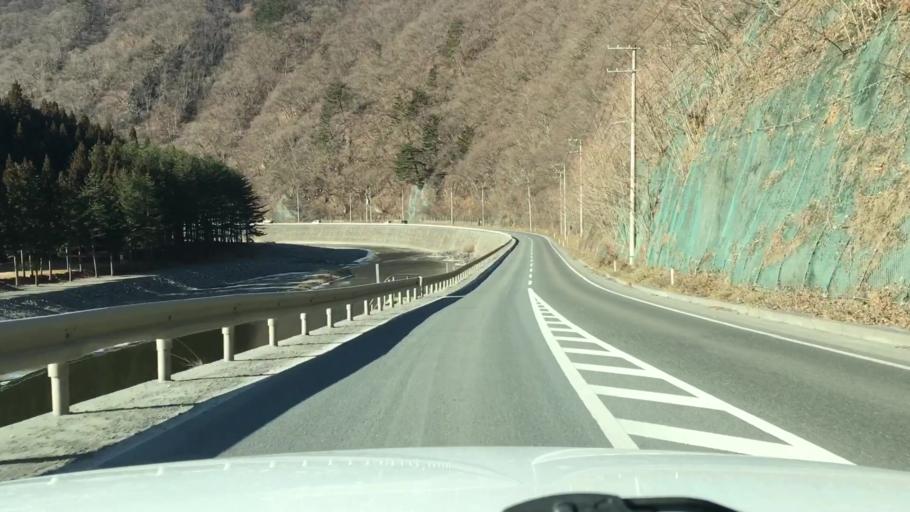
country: JP
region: Iwate
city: Miyako
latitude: 39.6165
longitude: 141.7961
